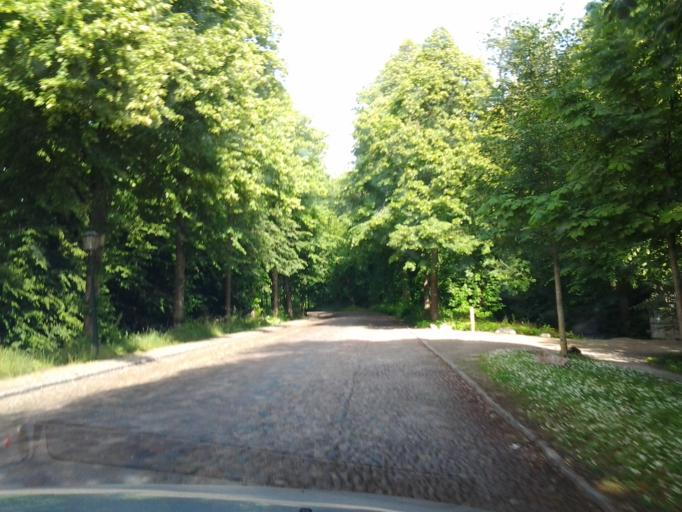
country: DE
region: Schleswig-Holstein
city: Aventoft
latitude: 54.9421
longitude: 8.8099
